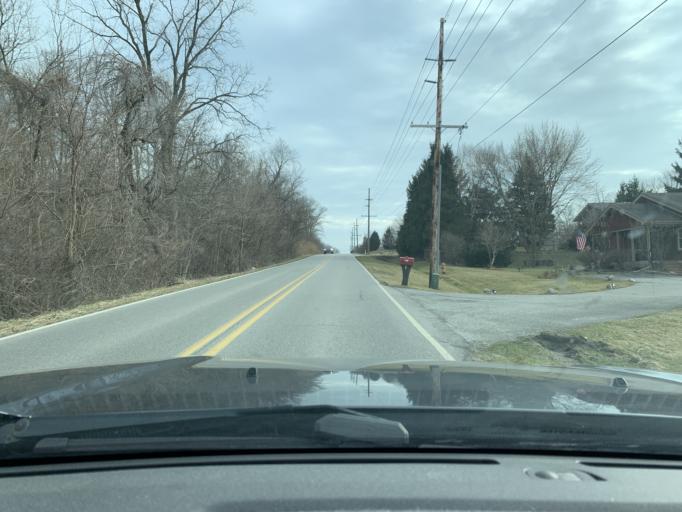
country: US
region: Indiana
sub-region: Porter County
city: Chesterton
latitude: 41.5532
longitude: -87.0664
